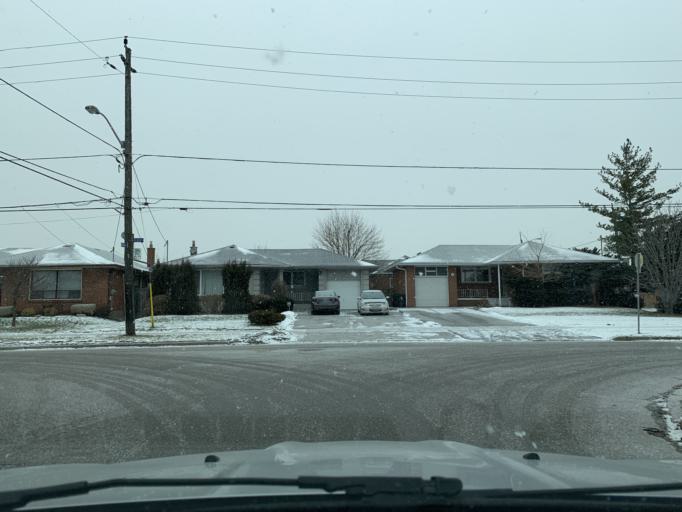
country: CA
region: Ontario
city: Concord
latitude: 43.7310
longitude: -79.4802
